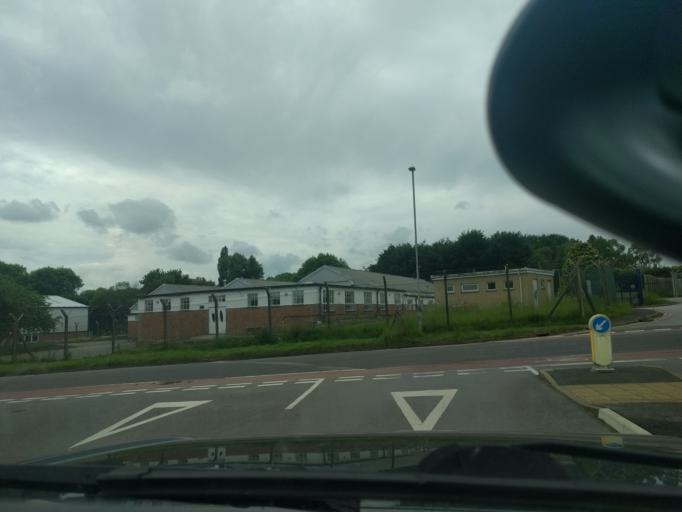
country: GB
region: England
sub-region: Wiltshire
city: Neston
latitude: 51.4193
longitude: -2.2142
